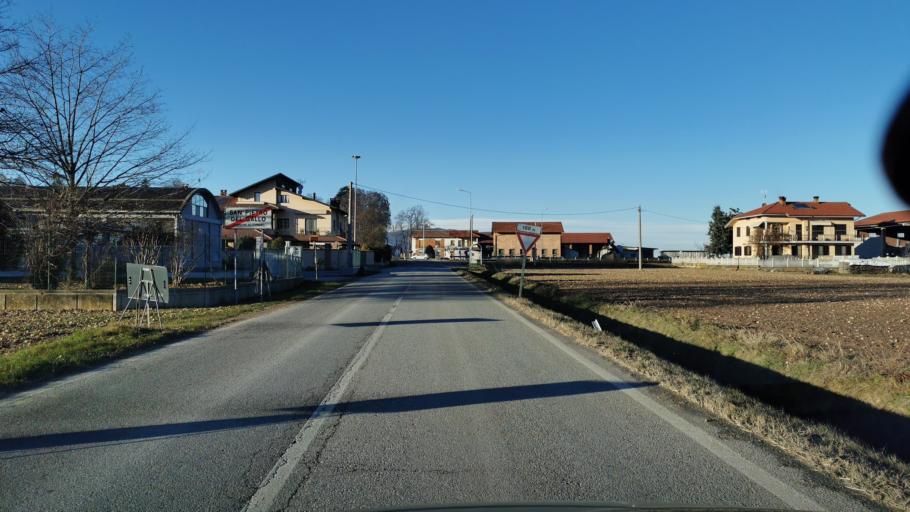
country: IT
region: Piedmont
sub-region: Provincia di Cuneo
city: Roata Rossi
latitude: 44.4556
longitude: 7.4894
